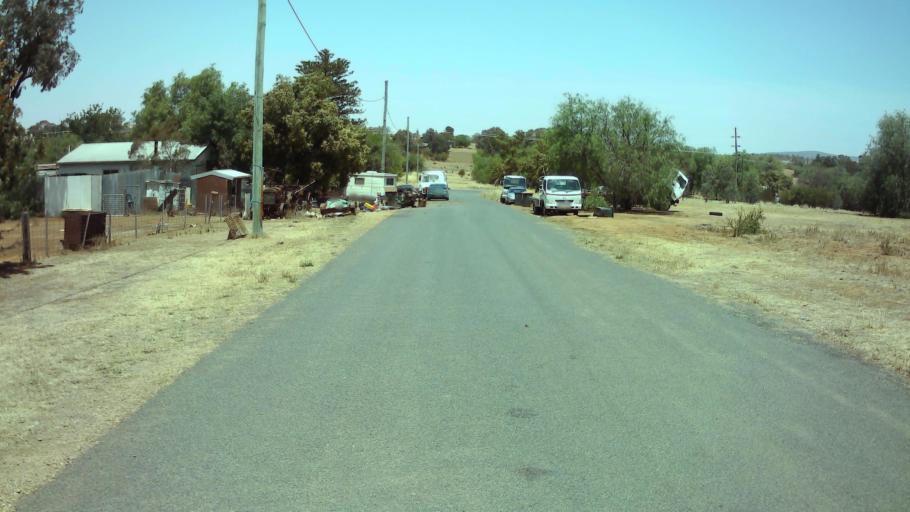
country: AU
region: New South Wales
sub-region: Weddin
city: Grenfell
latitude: -33.8968
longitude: 148.1710
